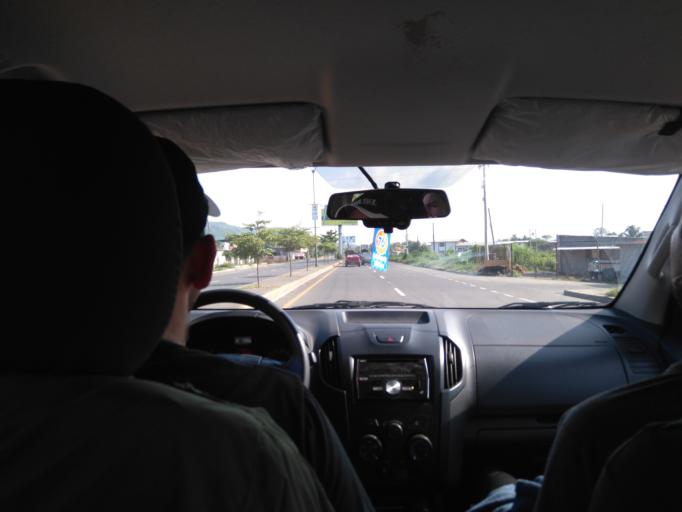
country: EC
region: Manabi
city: Portoviejo
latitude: -1.0002
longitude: -80.4664
